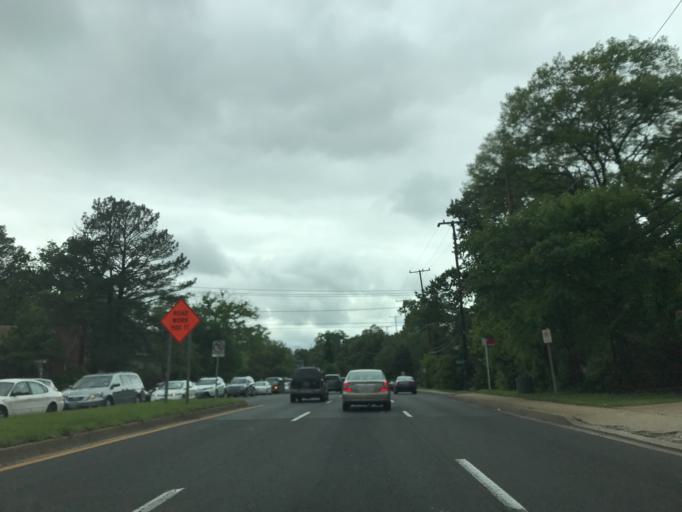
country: US
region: Maryland
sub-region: Prince George's County
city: University Park
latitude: 38.9653
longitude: -76.9410
